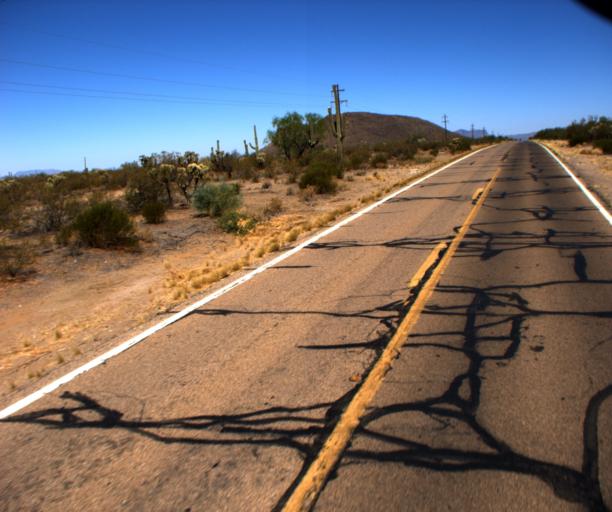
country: US
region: Arizona
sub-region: Pima County
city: Sells
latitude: 31.9422
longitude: -111.9243
